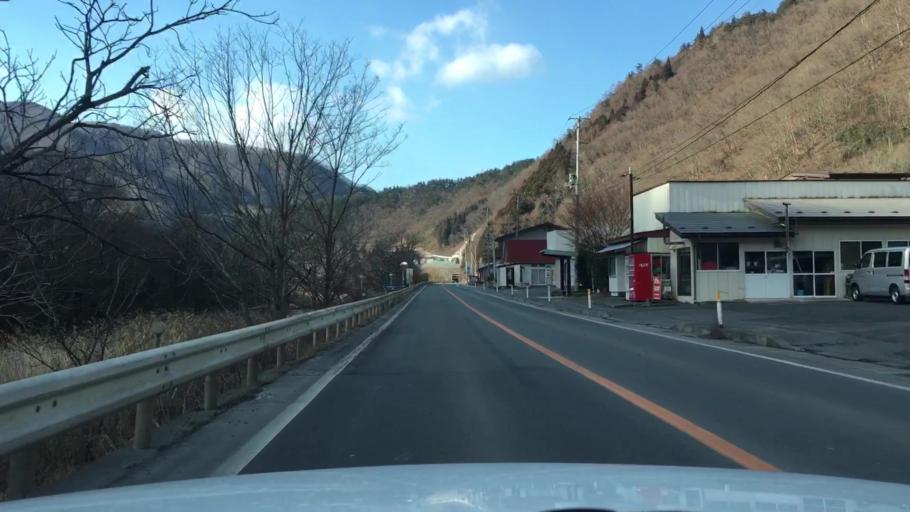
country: JP
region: Iwate
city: Miyako
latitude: 39.5930
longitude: 141.6638
